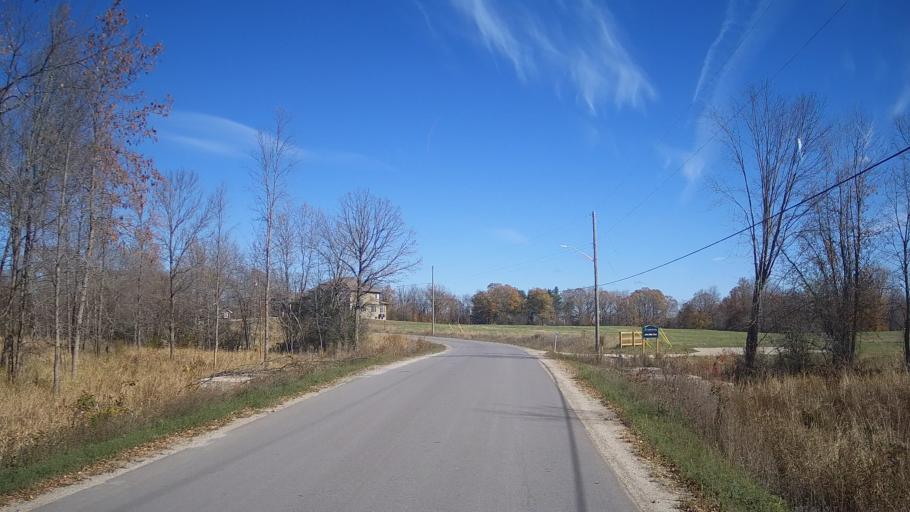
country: CA
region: Ontario
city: Perth
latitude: 44.8761
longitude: -76.2976
